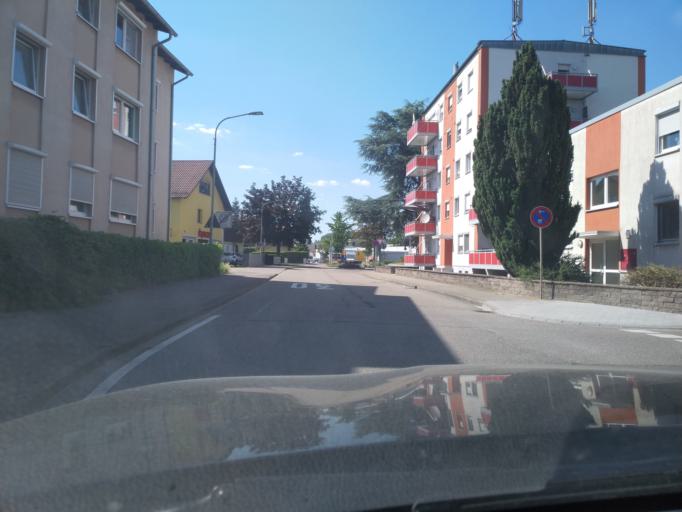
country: DE
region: Rheinland-Pfalz
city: Worth am Rhein
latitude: 49.0378
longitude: 8.2911
